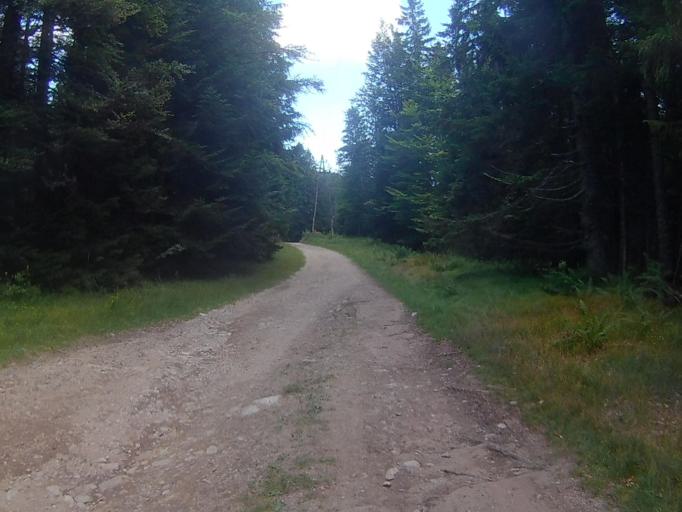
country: SI
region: Ruse
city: Ruse
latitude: 46.4954
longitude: 15.5215
